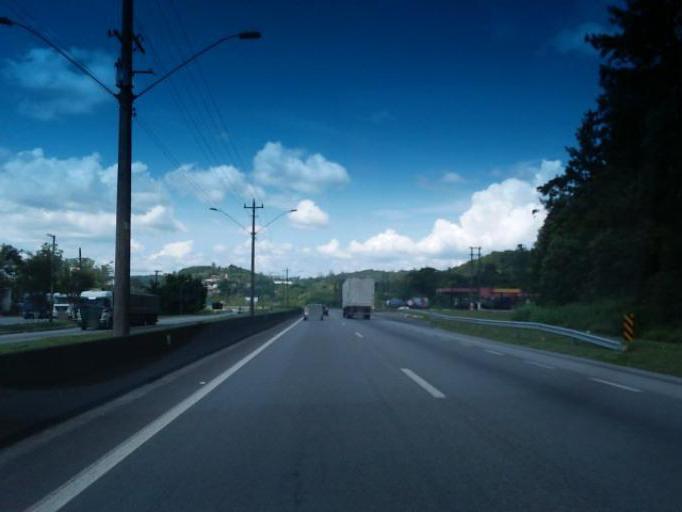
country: BR
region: Sao Paulo
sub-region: Sao Lourenco Da Serra
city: Sao Lourenco da Serra
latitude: -23.8900
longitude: -46.9815
